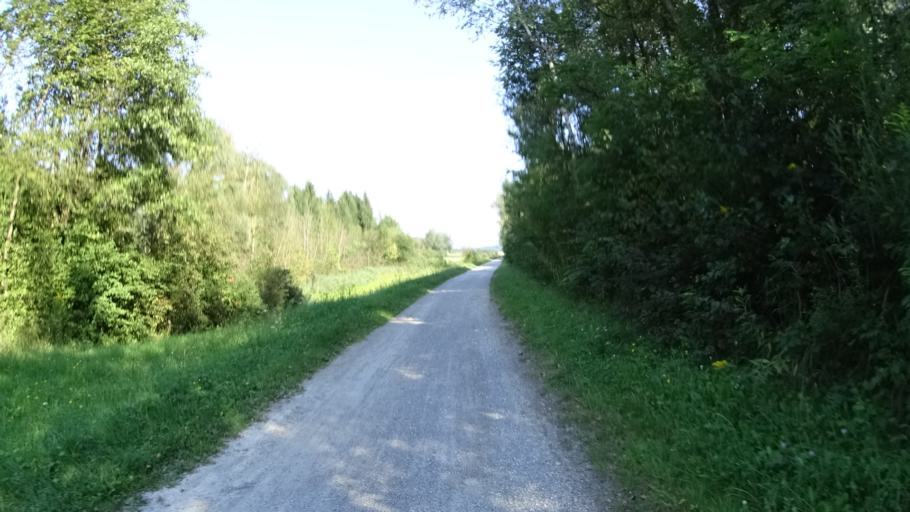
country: AT
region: Carinthia
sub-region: Politischer Bezirk Villach Land
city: Wernberg
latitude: 46.6144
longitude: 13.9284
